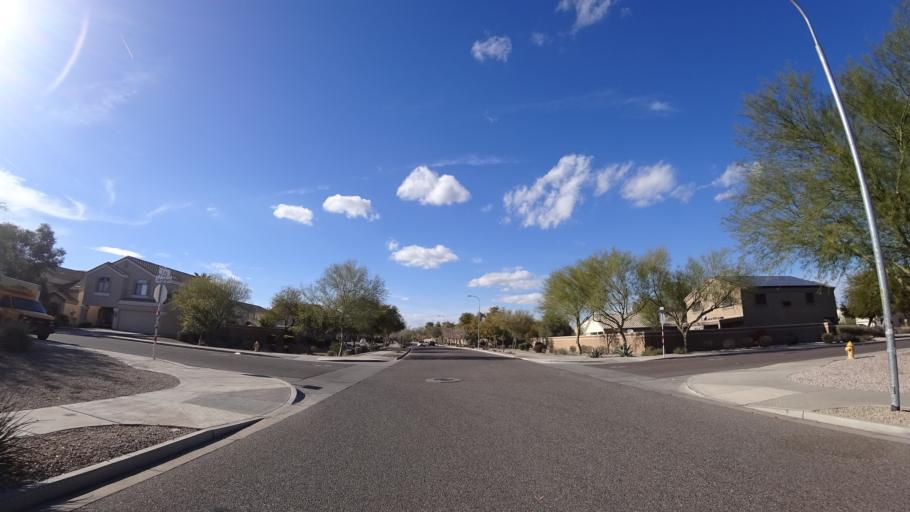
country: US
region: Arizona
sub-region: Maricopa County
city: Tolleson
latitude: 33.4188
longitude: -112.2433
